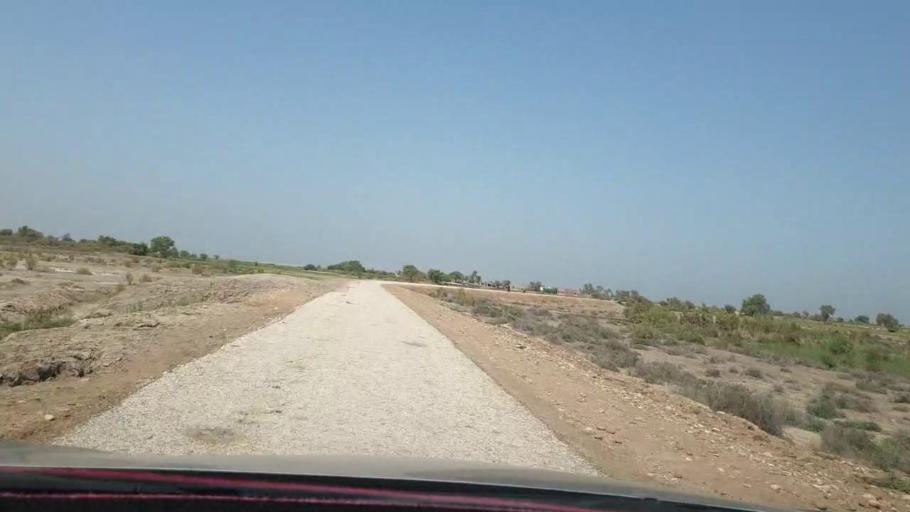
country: PK
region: Sindh
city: Warah
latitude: 27.5222
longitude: 67.7086
